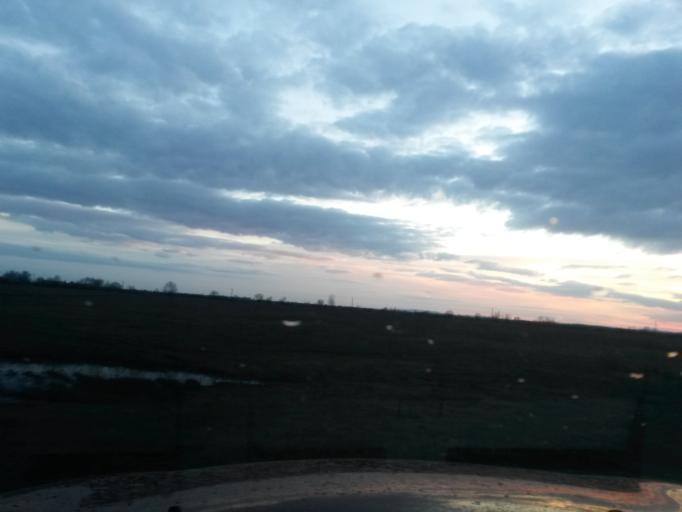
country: SK
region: Kosicky
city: Sobrance
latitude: 48.6953
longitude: 22.0551
